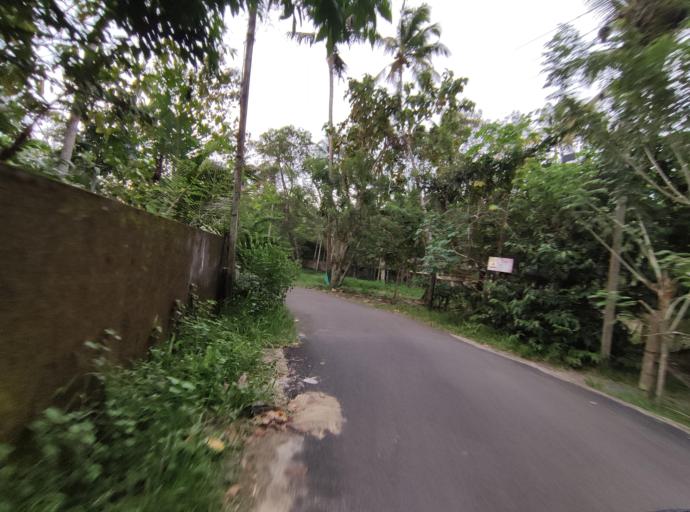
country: IN
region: Kerala
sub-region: Alappuzha
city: Shertallai
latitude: 9.6661
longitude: 76.3483
